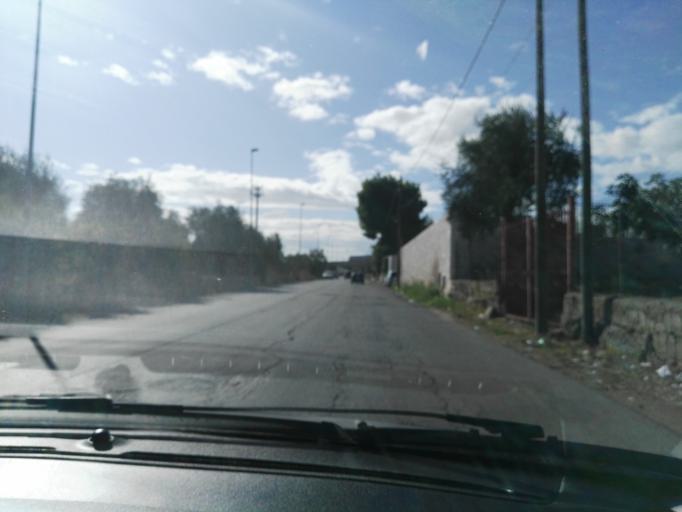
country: IT
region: Apulia
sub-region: Provincia di Bari
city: Triggiano
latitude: 41.0634
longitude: 16.9346
